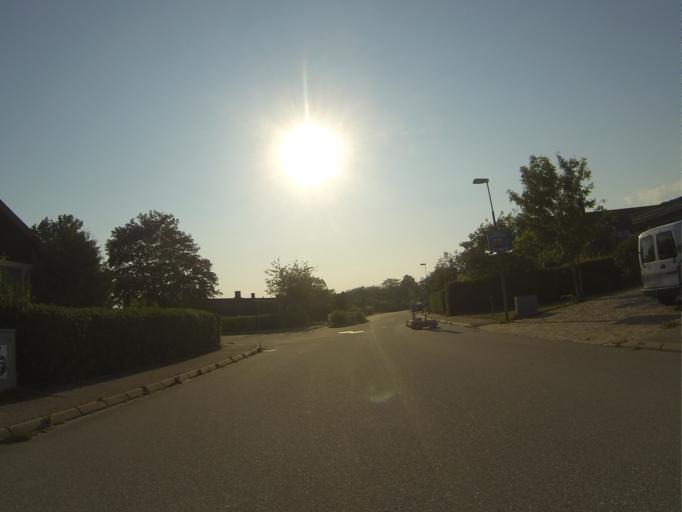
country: SE
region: Skane
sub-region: Lunds Kommun
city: Genarp
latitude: 55.6694
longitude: 13.3554
